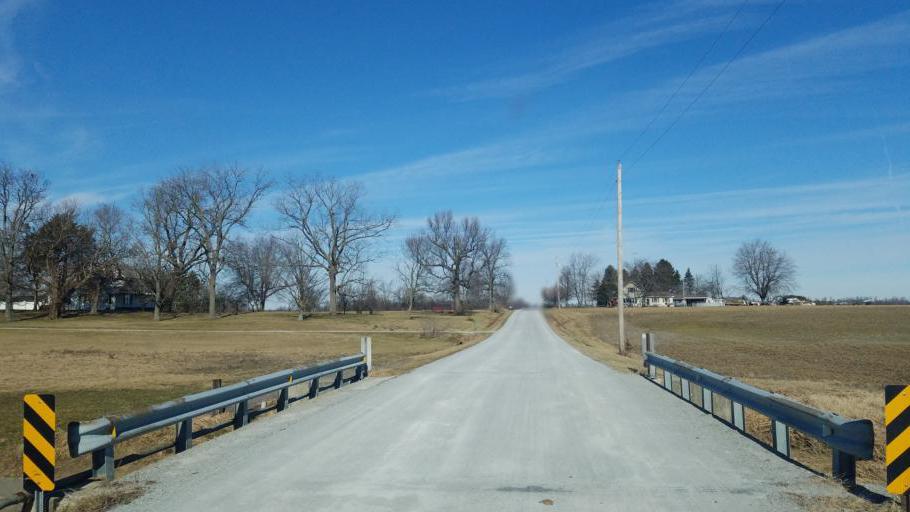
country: US
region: Ohio
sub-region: Hardin County
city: Kenton
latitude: 40.5697
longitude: -83.4684
